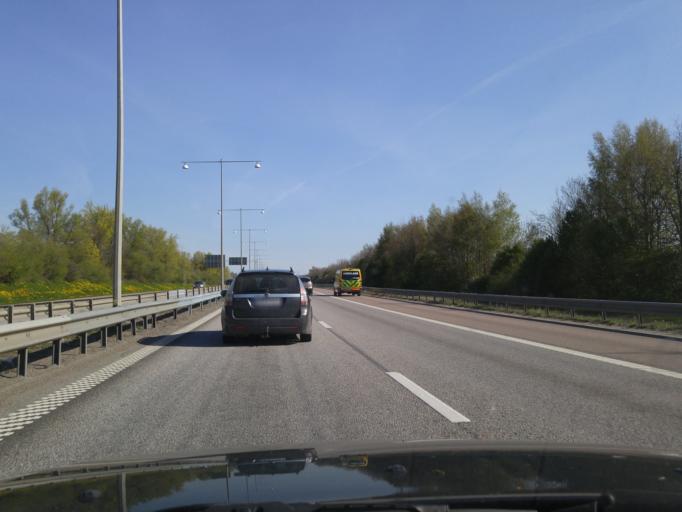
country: SE
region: Vaestra Goetaland
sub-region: Goteborg
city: Goeteborg
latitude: 57.7400
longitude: 11.9876
